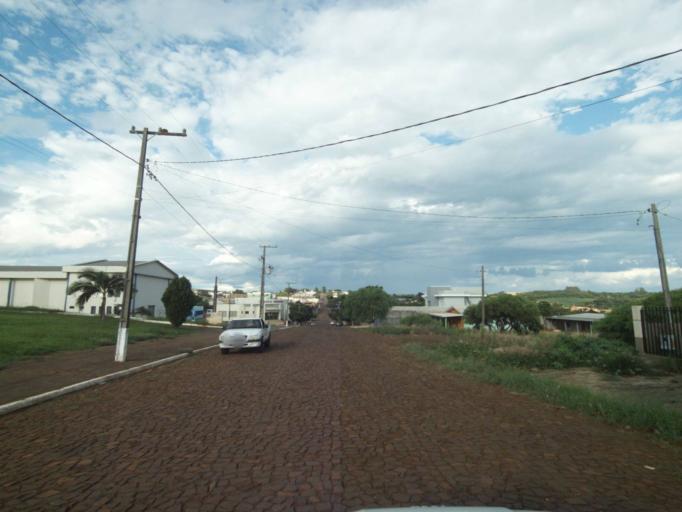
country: BR
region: Parana
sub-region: Laranjeiras Do Sul
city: Laranjeiras do Sul
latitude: -25.4953
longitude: -52.5324
